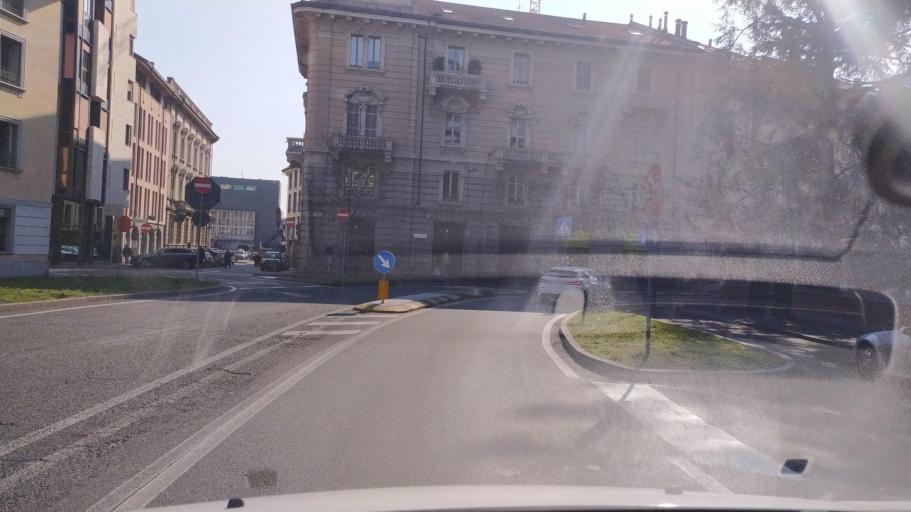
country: IT
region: Lombardy
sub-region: Provincia di Varese
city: Gallarate
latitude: 45.6622
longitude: 8.7920
